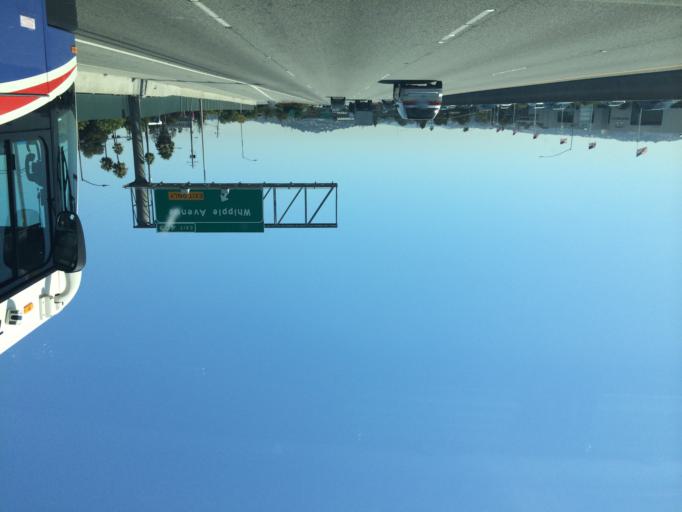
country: US
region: California
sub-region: San Mateo County
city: Redwood City
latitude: 37.4953
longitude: -122.2292
